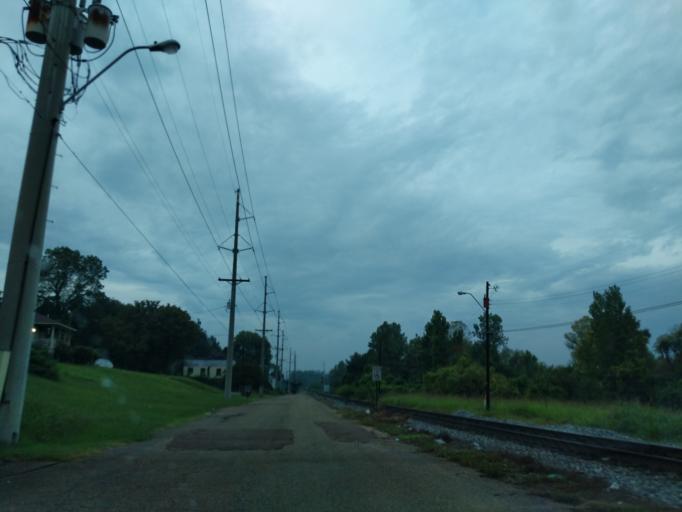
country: US
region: Mississippi
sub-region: Warren County
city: Vicksburg
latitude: 32.3396
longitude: -90.8881
